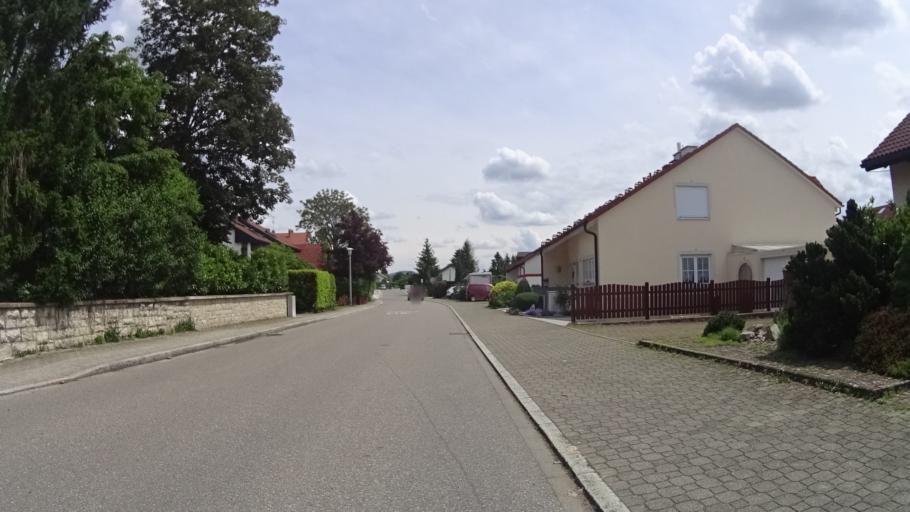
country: DE
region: Baden-Wuerttemberg
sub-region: Freiburg Region
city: Grenzach-Wyhlen
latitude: 47.5438
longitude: 7.6891
